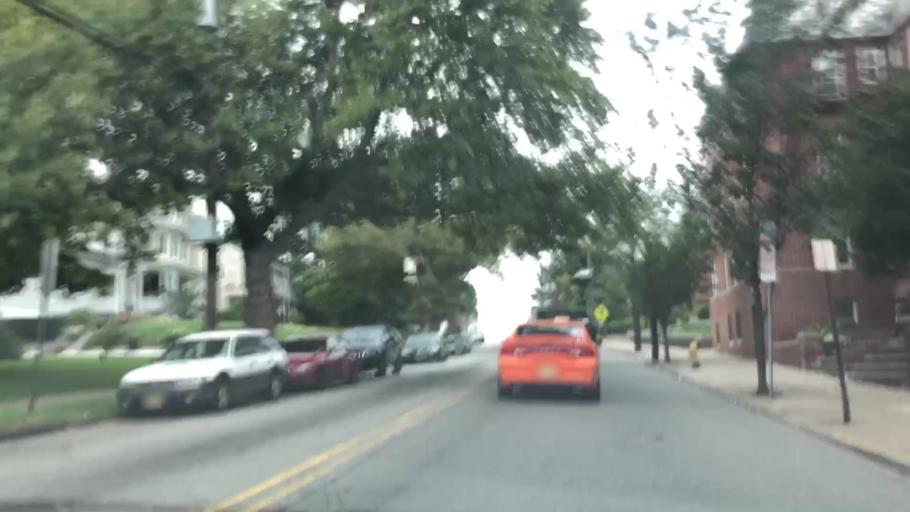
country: US
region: New Jersey
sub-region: Essex County
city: Bloomfield
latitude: 40.7871
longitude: -74.1875
